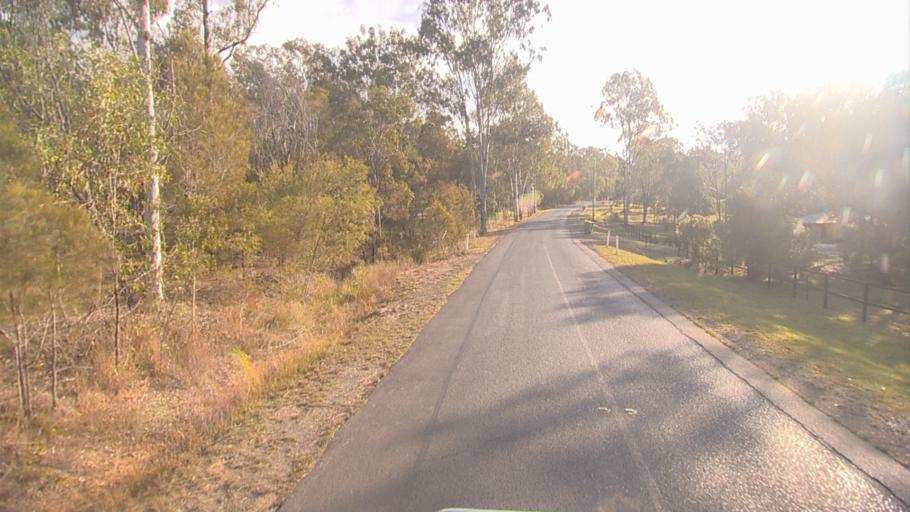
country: AU
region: Queensland
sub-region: Logan
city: Cedar Vale
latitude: -27.8484
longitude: 153.0995
